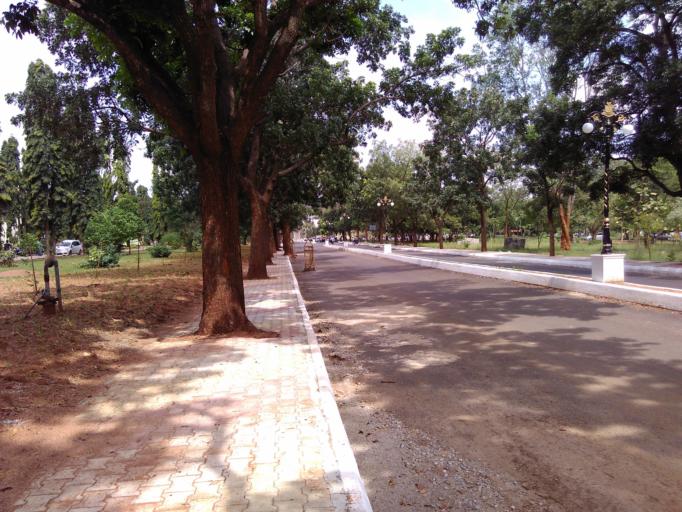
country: IN
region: Karnataka
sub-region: Mysore
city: Mysore
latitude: 12.3100
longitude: 76.6239
